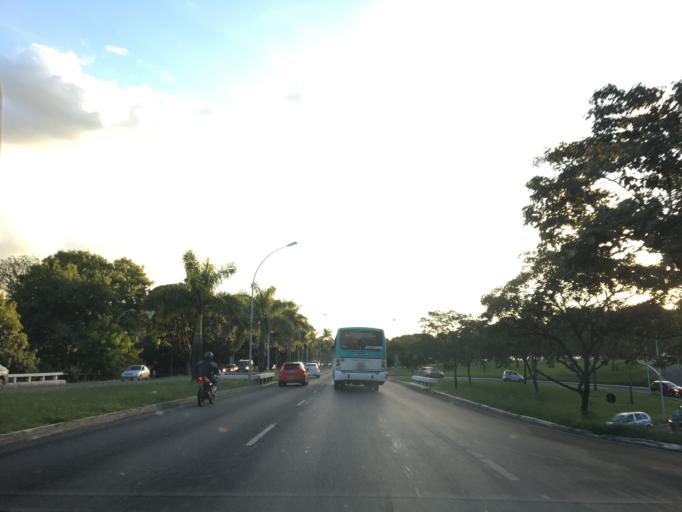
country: BR
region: Federal District
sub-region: Brasilia
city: Brasilia
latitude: -15.8292
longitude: -47.9167
